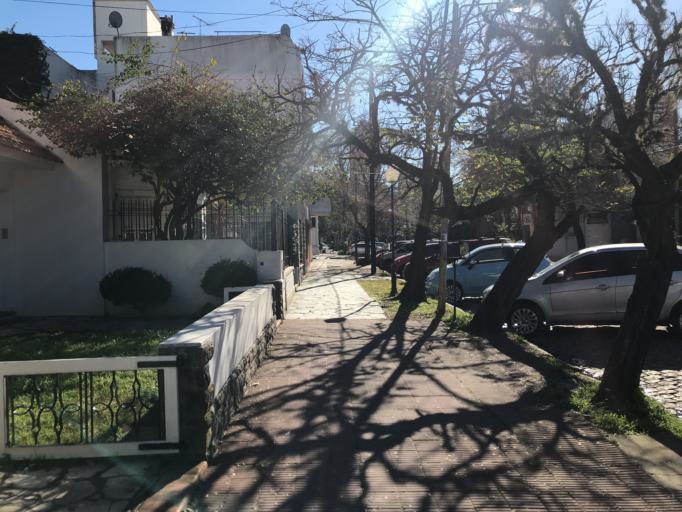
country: AR
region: Buenos Aires
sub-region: Partido de Lomas de Zamora
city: Lomas de Zamora
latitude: -34.7680
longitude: -58.4003
